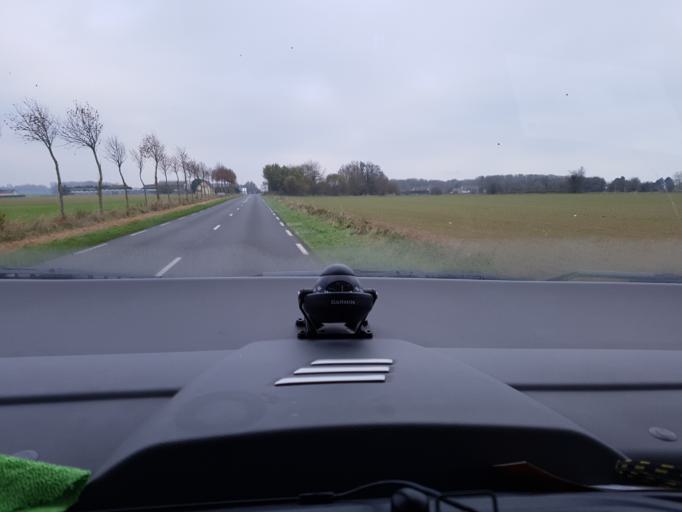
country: FR
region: Picardie
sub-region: Departement de la Somme
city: Ault
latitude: 50.0986
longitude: 1.4673
